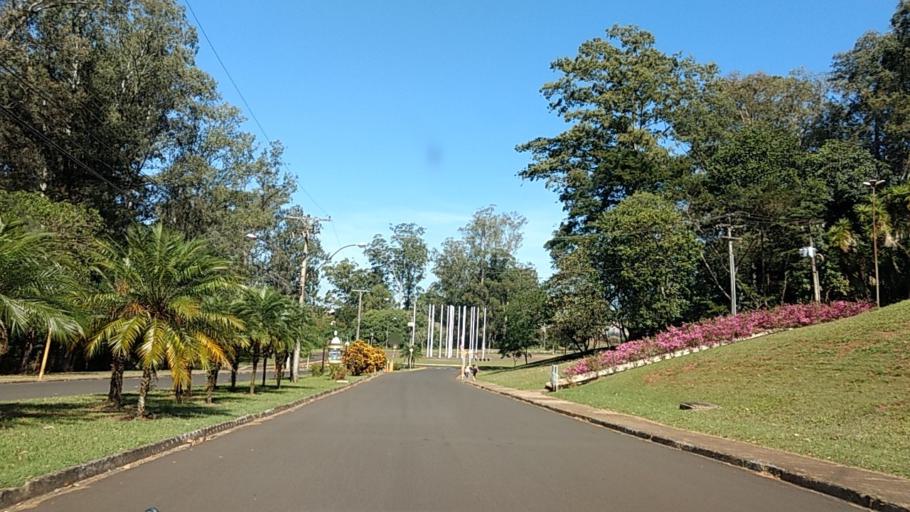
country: BR
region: Sao Paulo
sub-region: Botucatu
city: Botucatu
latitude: -22.8548
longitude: -48.4324
